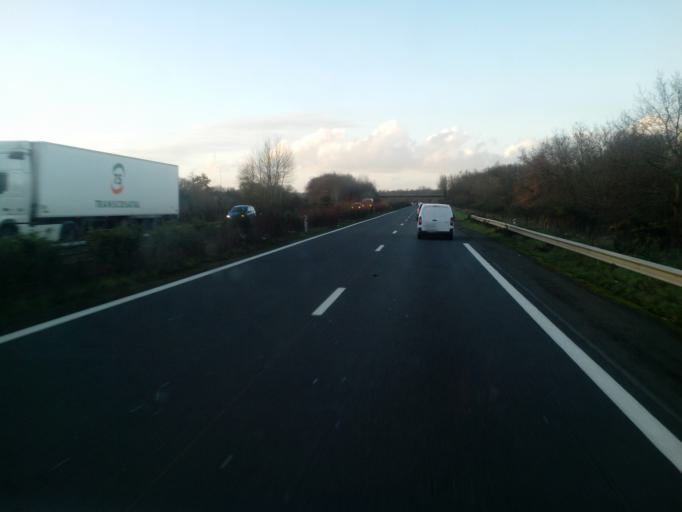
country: FR
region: Pays de la Loire
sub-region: Departement de la Loire-Atlantique
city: La Haie-Fouassiere
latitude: 47.1644
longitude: -1.3686
